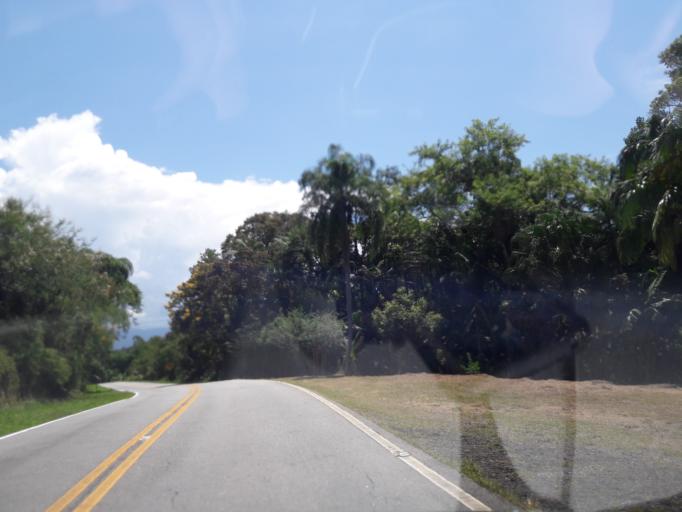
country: BR
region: Parana
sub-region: Antonina
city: Antonina
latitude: -25.5259
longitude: -48.7901
